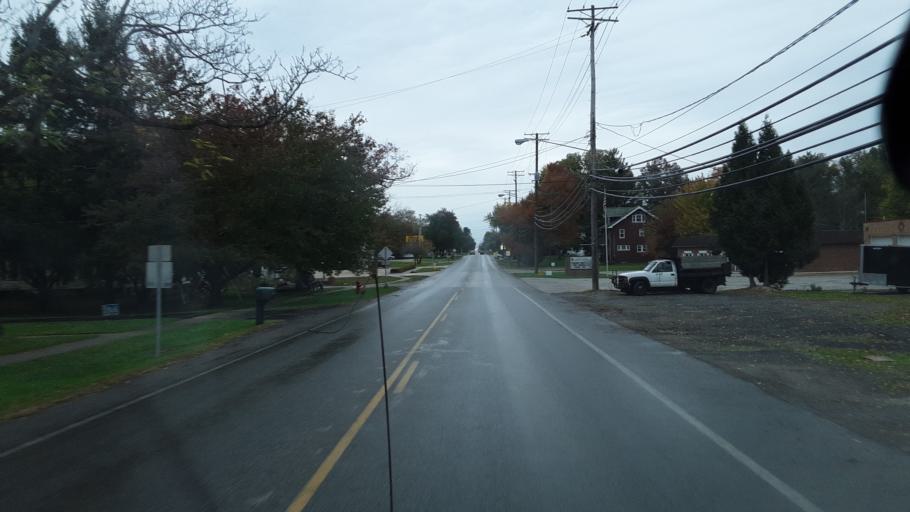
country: US
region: Ohio
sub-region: Ashtabula County
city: Orwell
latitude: 41.5351
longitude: -80.8658
